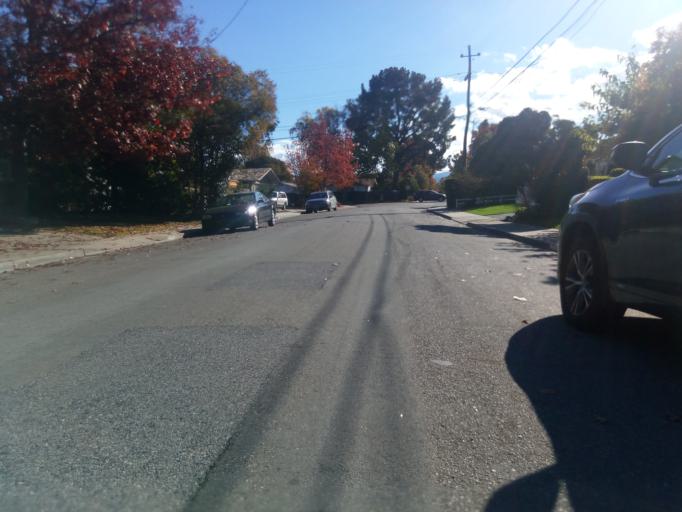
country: US
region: California
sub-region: Santa Clara County
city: Mountain View
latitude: 37.3799
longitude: -122.0795
